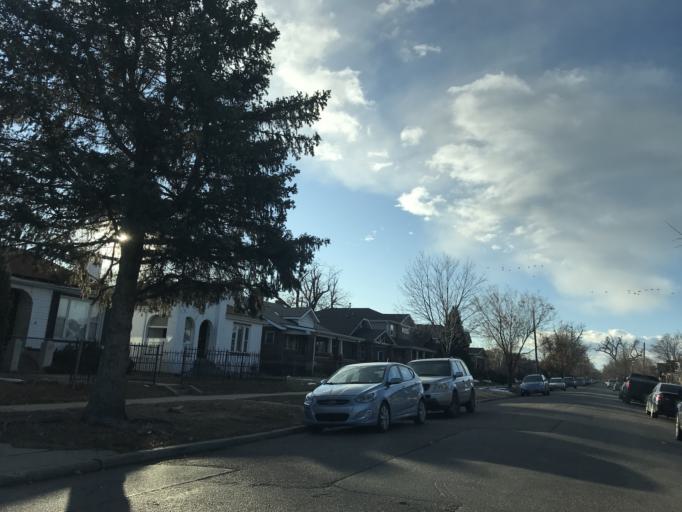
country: US
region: Colorado
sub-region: Denver County
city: Denver
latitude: 39.7644
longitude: -104.9623
